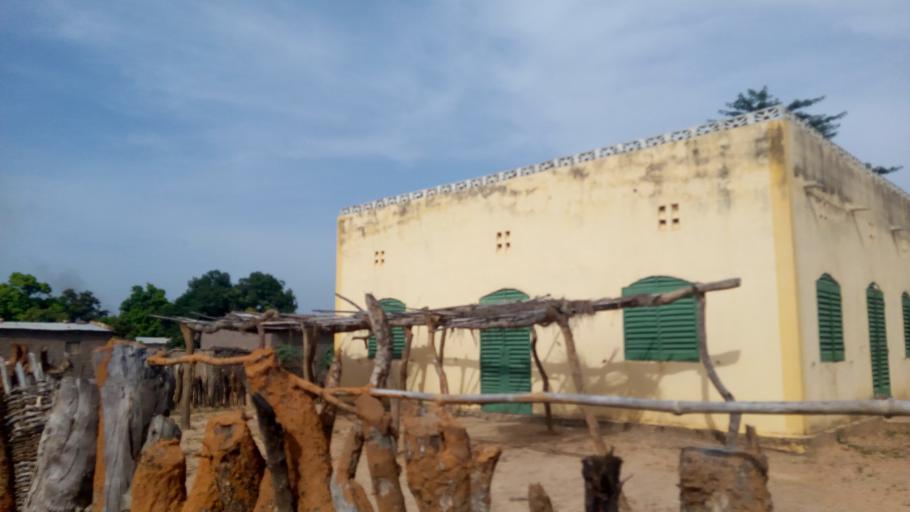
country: ML
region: Kayes
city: Kita
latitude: 13.1418
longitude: -8.8664
